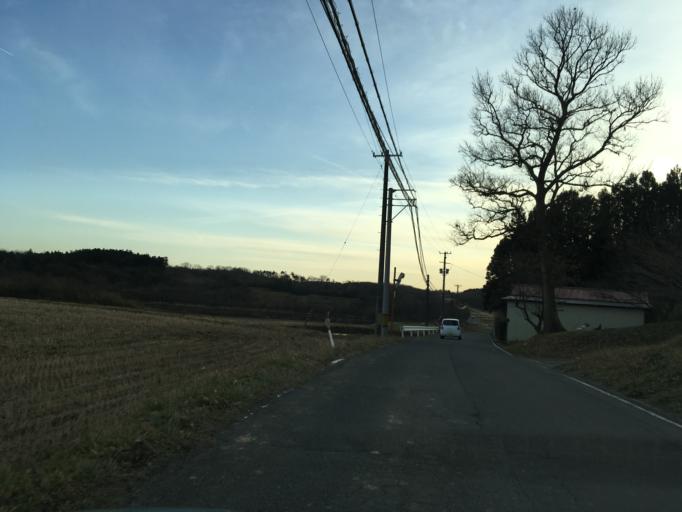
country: JP
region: Miyagi
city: Kogota
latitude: 38.6815
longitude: 141.0943
